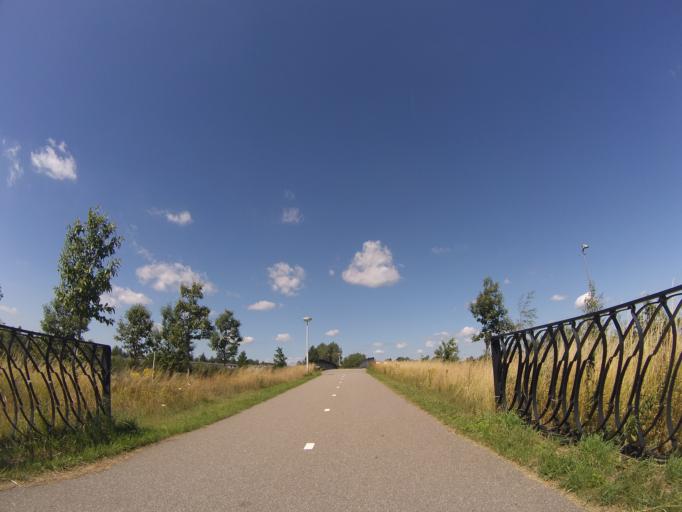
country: NL
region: Utrecht
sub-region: Stichtse Vecht
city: Spechtenkamp
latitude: 52.1104
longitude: 5.0283
